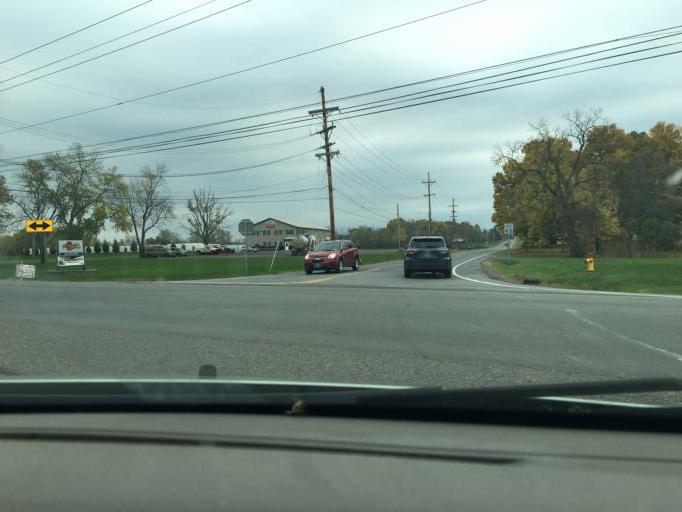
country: US
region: New York
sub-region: Ontario County
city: Manchester
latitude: 42.9726
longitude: -77.3193
